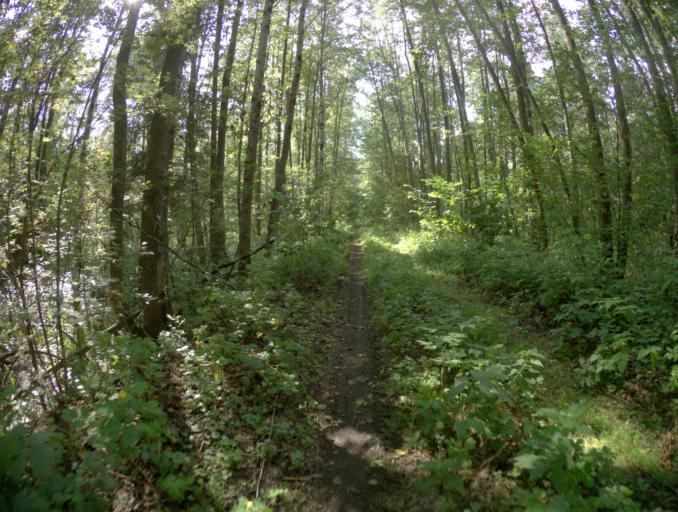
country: RU
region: Vladimir
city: Sobinka
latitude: 55.9093
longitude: 40.1245
